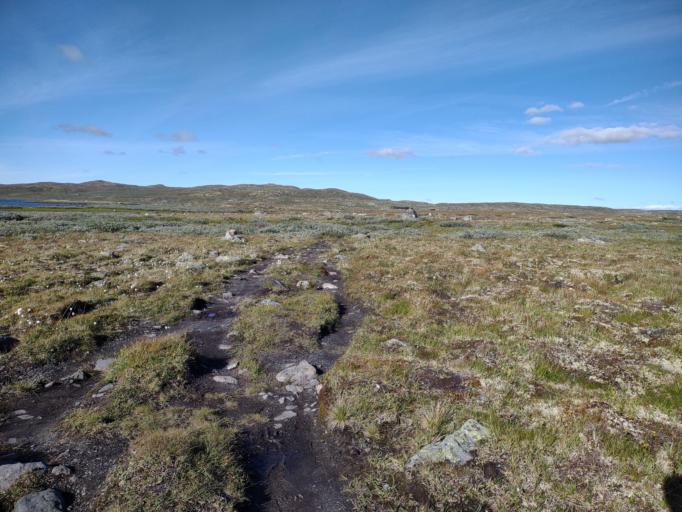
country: NO
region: Hordaland
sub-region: Eidfjord
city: Eidfjord
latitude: 60.1749
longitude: 7.4631
